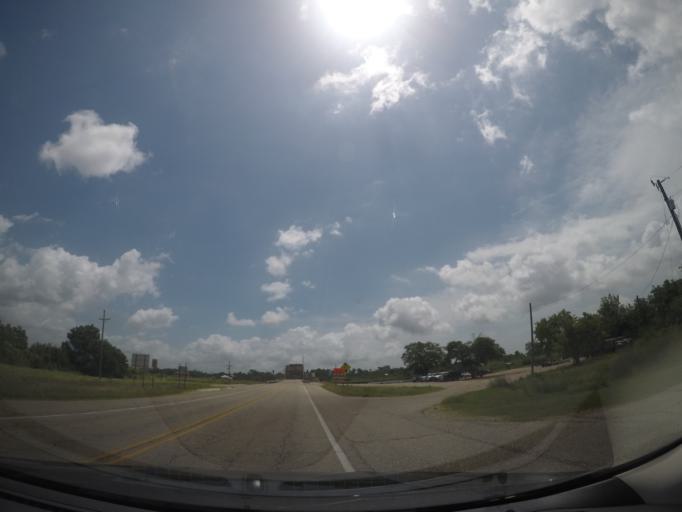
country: US
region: Mississippi
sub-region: Hancock County
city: Pearlington
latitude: 30.2387
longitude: -89.6173
